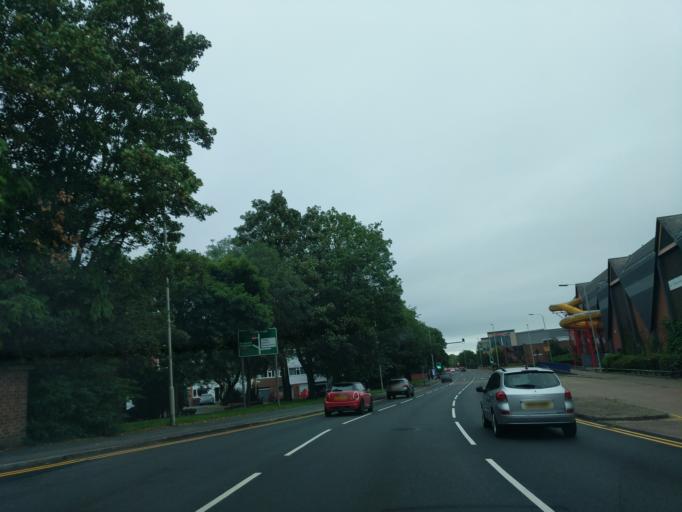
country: GB
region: England
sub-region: Dudley
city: Stourbridge
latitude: 52.4553
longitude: -2.1497
